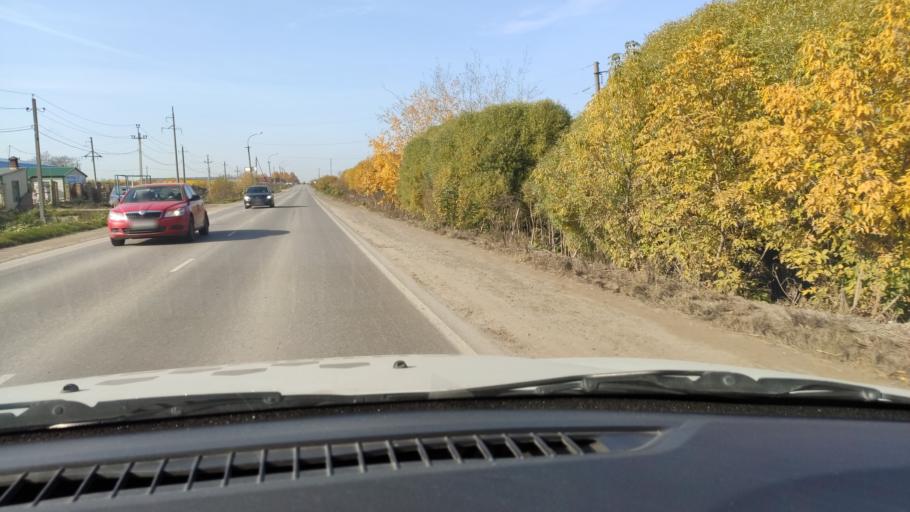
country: RU
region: Perm
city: Sylva
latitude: 58.0274
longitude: 56.7229
